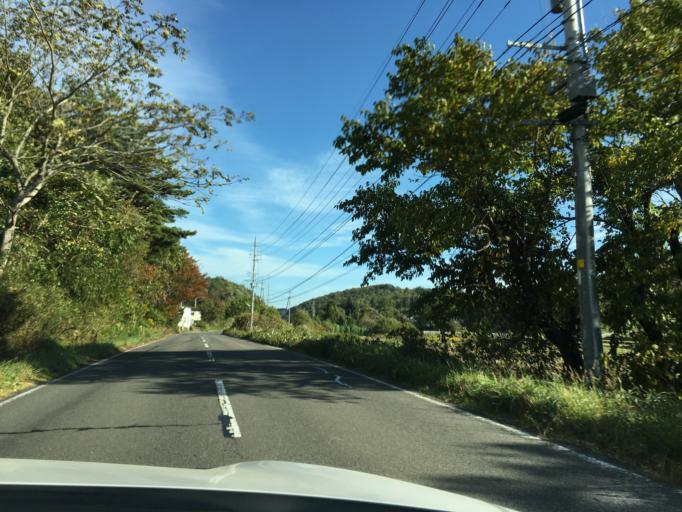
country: JP
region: Fukushima
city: Funehikimachi-funehiki
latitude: 37.3372
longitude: 140.5727
